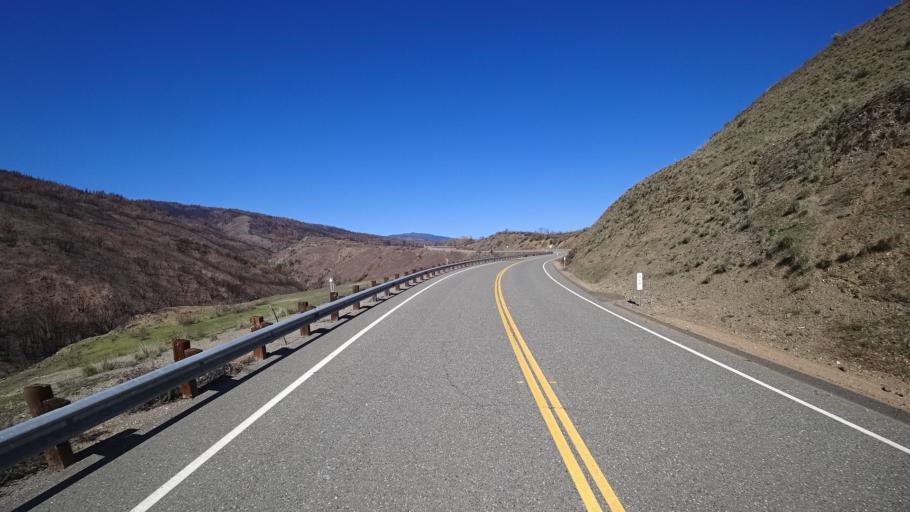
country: US
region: California
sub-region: Tehama County
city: Rancho Tehama Reserve
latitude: 39.6649
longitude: -122.6648
